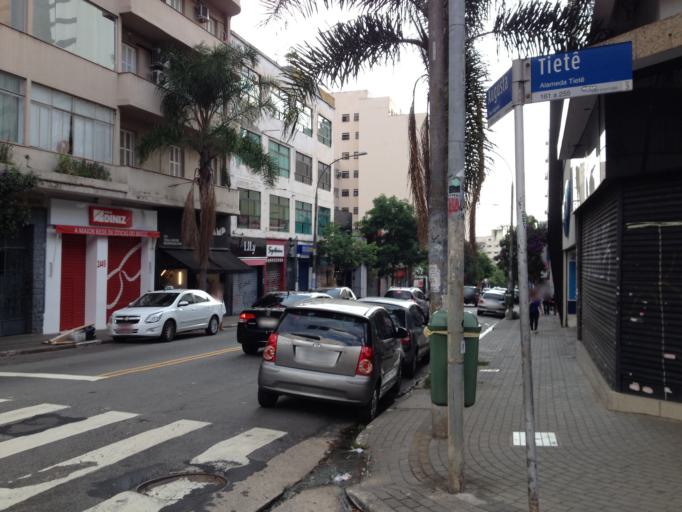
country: BR
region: Sao Paulo
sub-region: Sao Paulo
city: Sao Paulo
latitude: -23.5628
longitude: -46.6650
